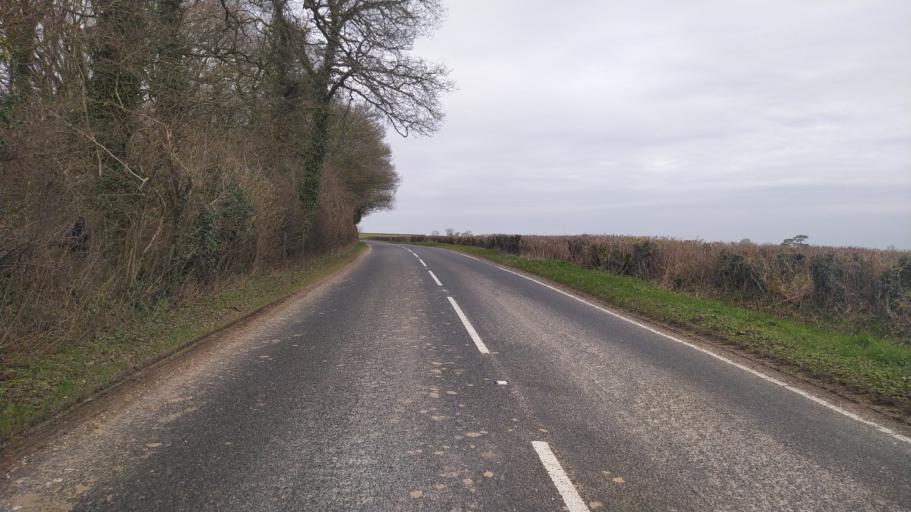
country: GB
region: England
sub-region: Dorset
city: Beaminster
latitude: 50.8206
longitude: -2.6639
